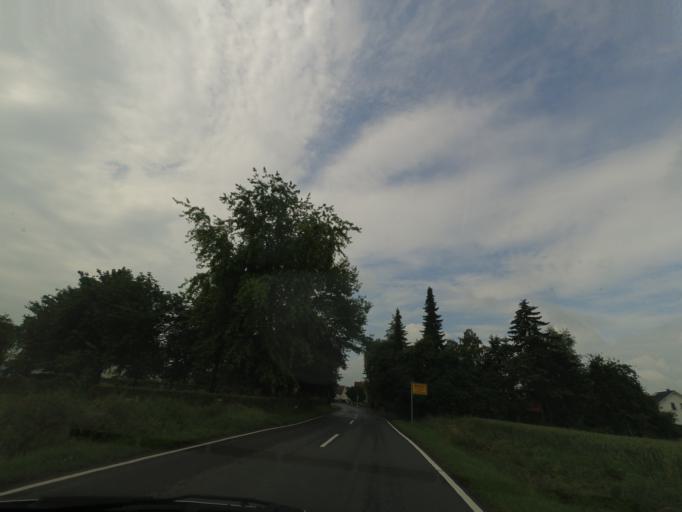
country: DE
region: Hesse
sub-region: Regierungsbezirk Giessen
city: Fronhausen
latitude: 50.7489
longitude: 8.7194
